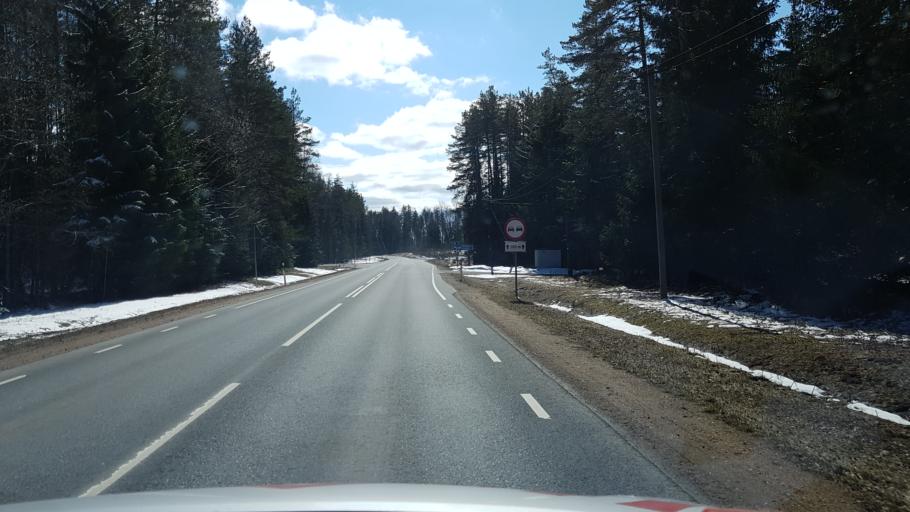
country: EE
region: Laeaene-Virumaa
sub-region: Kadrina vald
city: Kadrina
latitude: 59.3962
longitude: 26.0133
